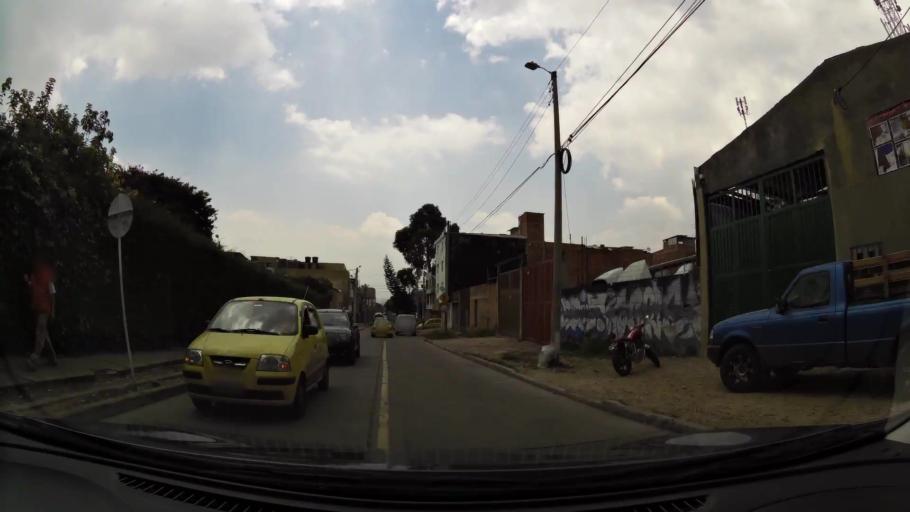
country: CO
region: Cundinamarca
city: La Calera
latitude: 4.7302
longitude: -74.0258
